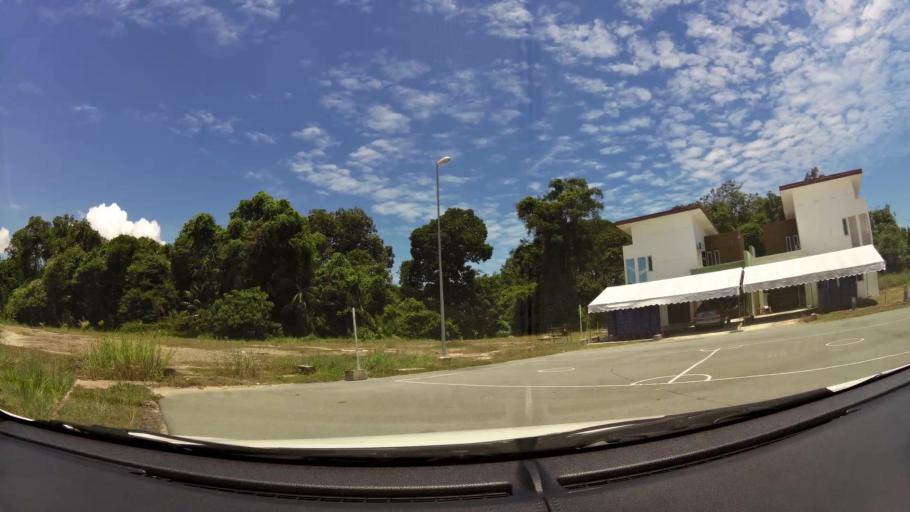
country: BN
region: Brunei and Muara
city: Bandar Seri Begawan
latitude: 5.0065
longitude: 115.0041
